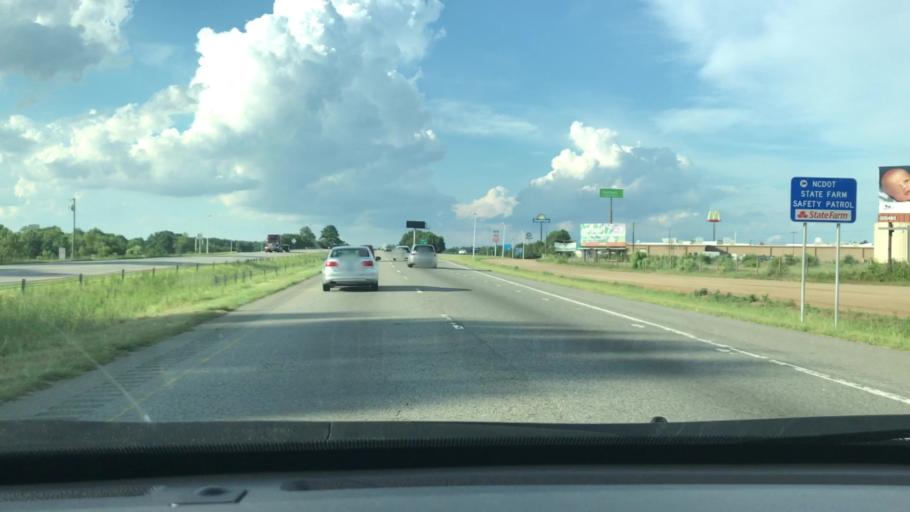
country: US
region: North Carolina
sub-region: Robeson County
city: Saint Pauls
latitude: 34.8066
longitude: -78.9881
